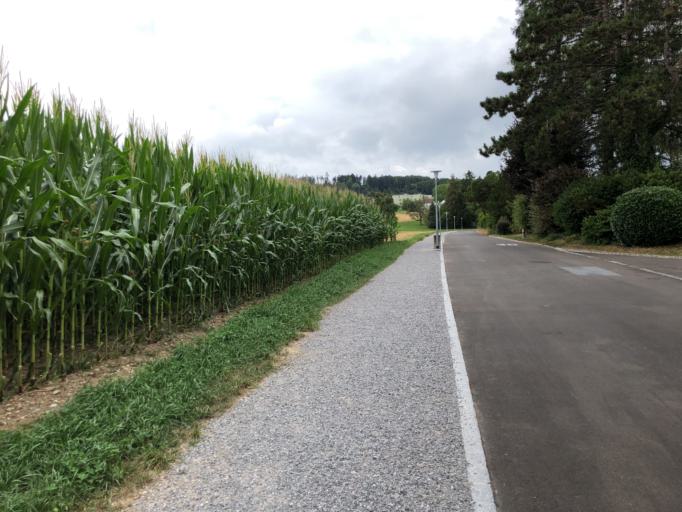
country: CH
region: Zurich
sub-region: Bezirk Uster
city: Pfaffhausen
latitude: 47.3664
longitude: 8.6268
